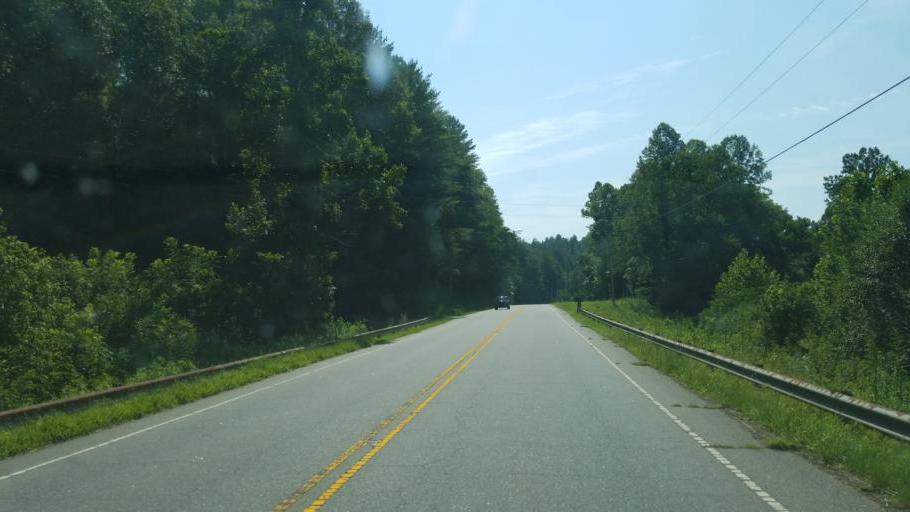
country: US
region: North Carolina
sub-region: Burke County
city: Glen Alpine
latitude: 35.8499
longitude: -81.7765
